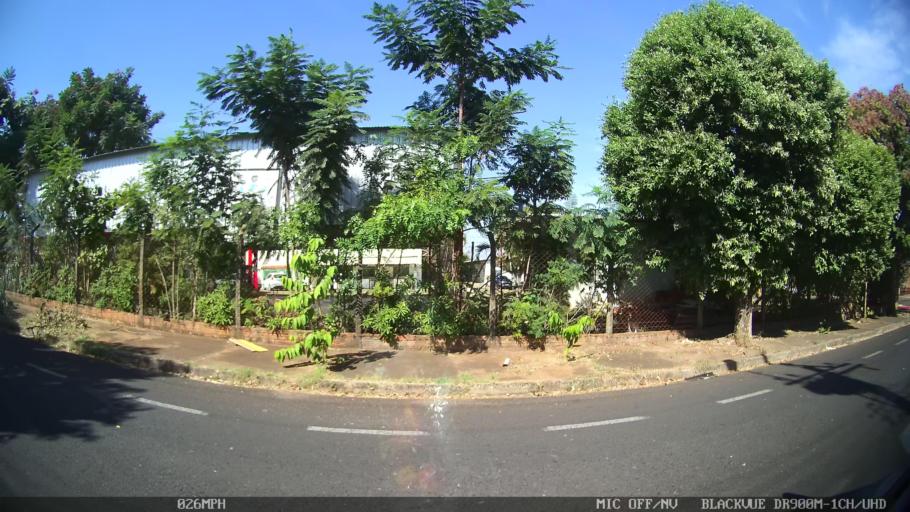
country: BR
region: Sao Paulo
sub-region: Sao Jose Do Rio Preto
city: Sao Jose do Rio Preto
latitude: -20.7845
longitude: -49.4128
